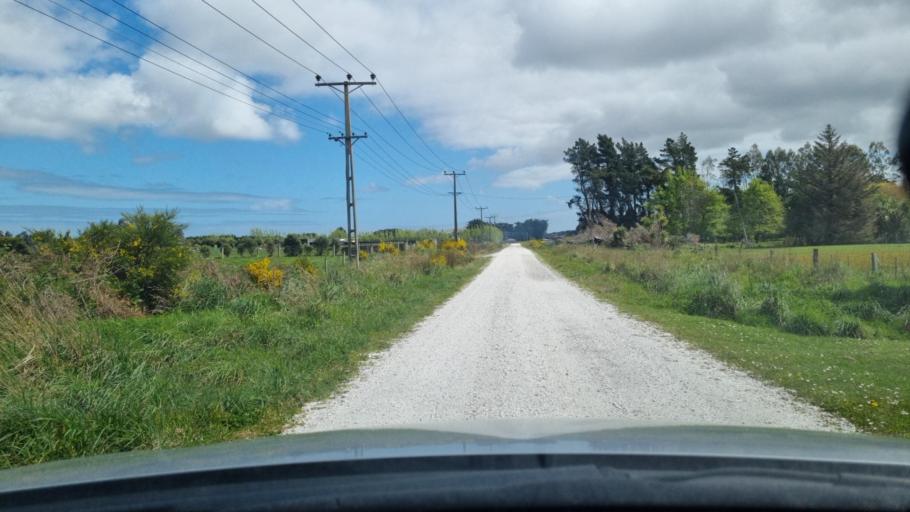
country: NZ
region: Southland
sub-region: Invercargill City
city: Invercargill
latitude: -46.4431
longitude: 168.3894
